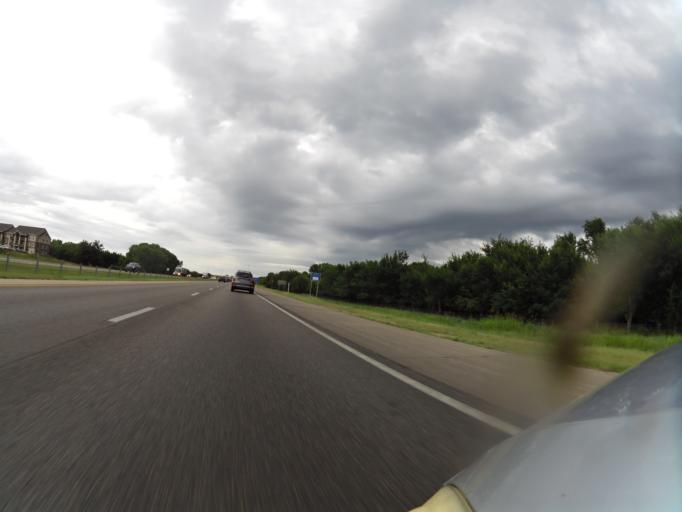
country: US
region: Kansas
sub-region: Sedgwick County
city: Bellaire
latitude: 37.7454
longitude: -97.2737
